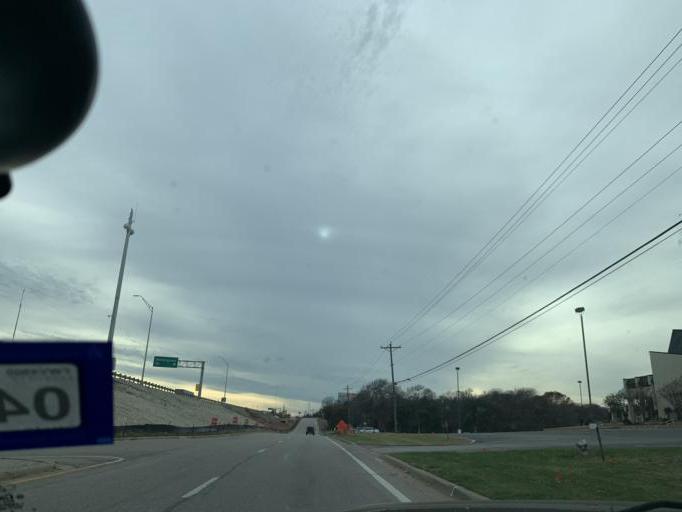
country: US
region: Texas
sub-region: Dallas County
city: Duncanville
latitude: 32.6255
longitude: -96.9087
